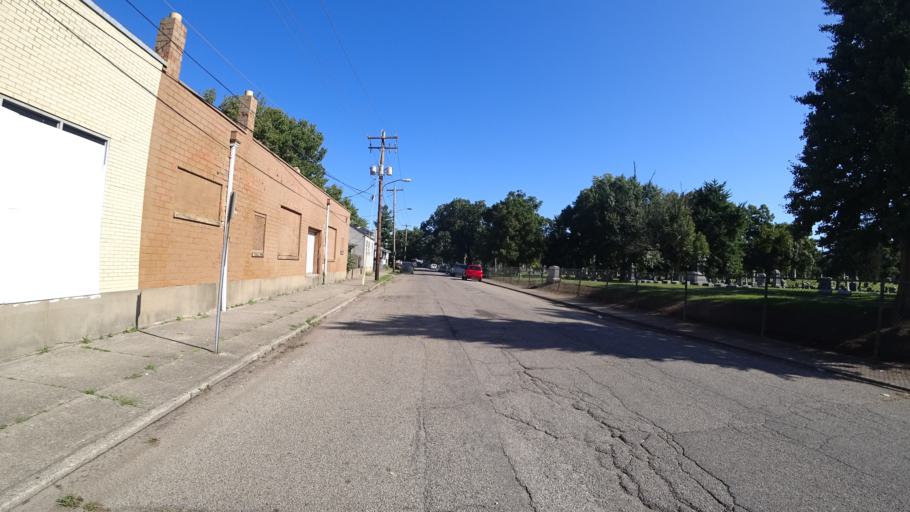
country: US
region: Ohio
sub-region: Butler County
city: Hamilton
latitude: 39.4011
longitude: -84.5476
